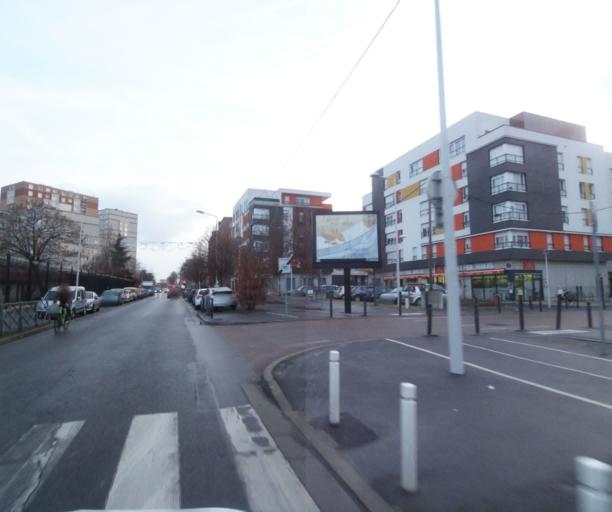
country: FR
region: Ile-de-France
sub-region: Departement du Val-d'Oise
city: Bezons
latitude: 48.9125
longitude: 2.2245
